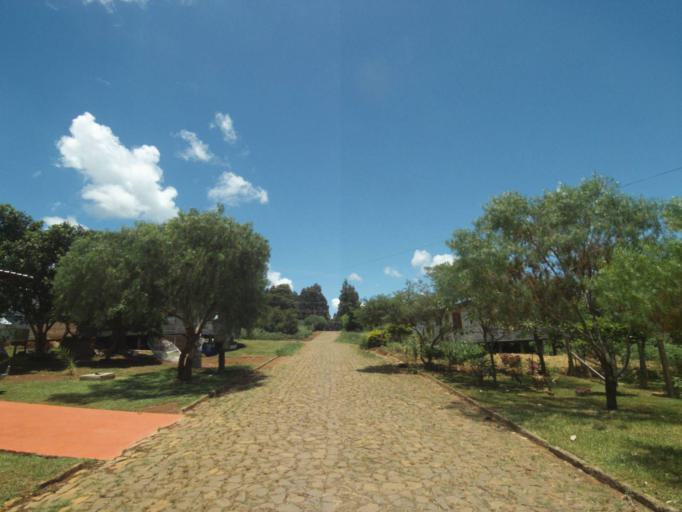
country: BR
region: Parana
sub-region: Pinhao
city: Pinhao
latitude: -25.7874
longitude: -52.0870
